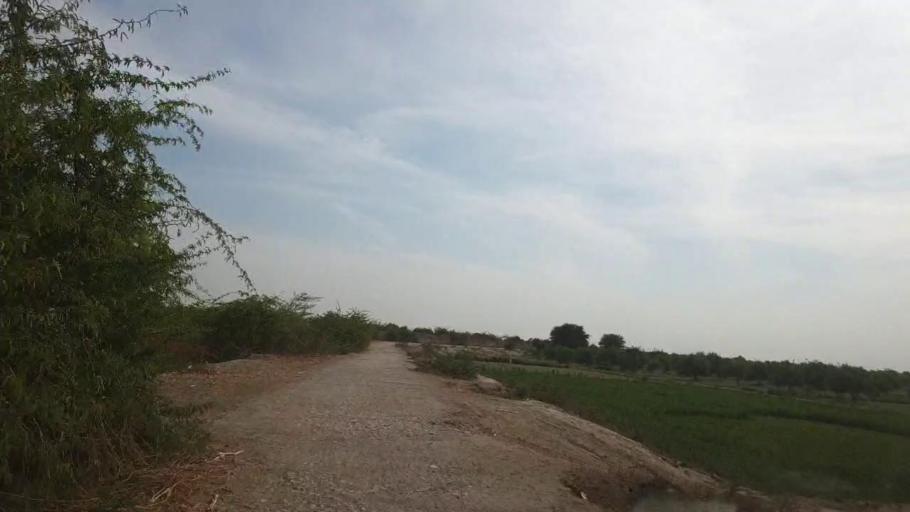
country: PK
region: Sindh
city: Nabisar
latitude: 24.9981
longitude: 69.5595
